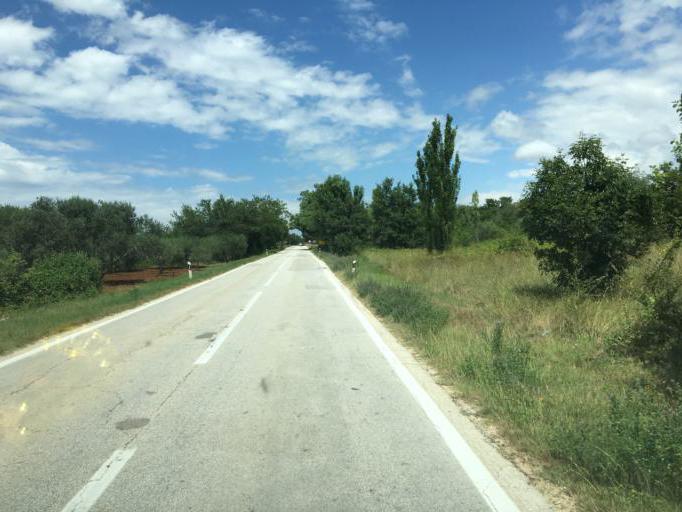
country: HR
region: Istarska
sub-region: Grad Rovinj
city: Rovinj
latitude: 45.1721
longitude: 13.7419
